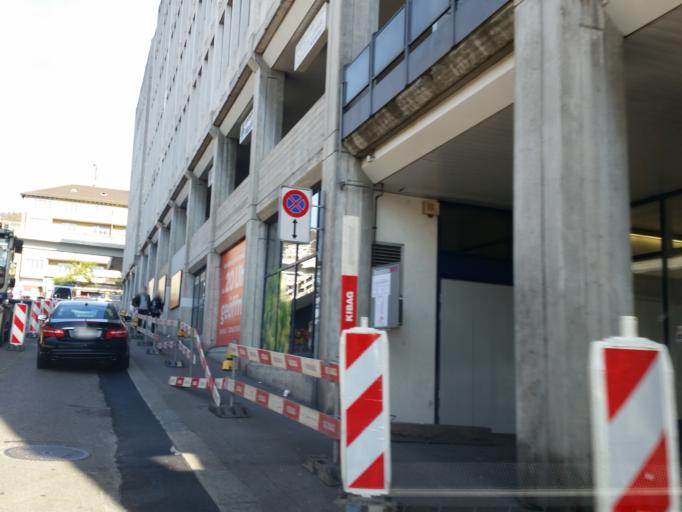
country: CH
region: Zurich
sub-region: Bezirk Zuerich
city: Zuerich (Kreis 10) / Wipkingen
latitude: 47.3925
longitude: 8.5244
